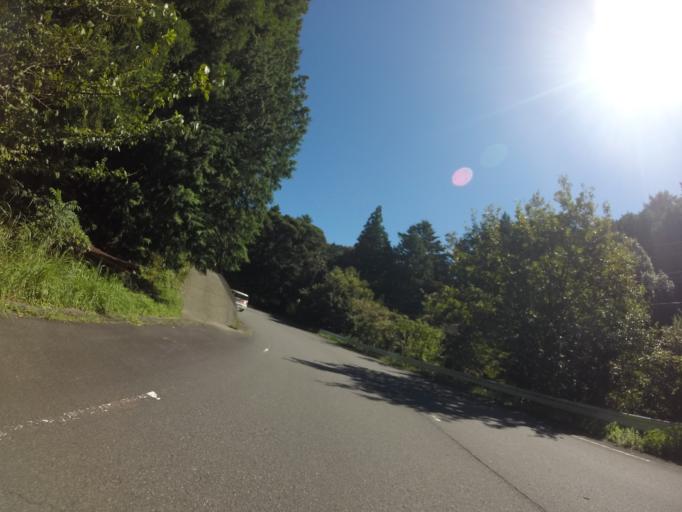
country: JP
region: Shizuoka
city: Kanaya
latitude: 34.9045
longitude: 138.1194
